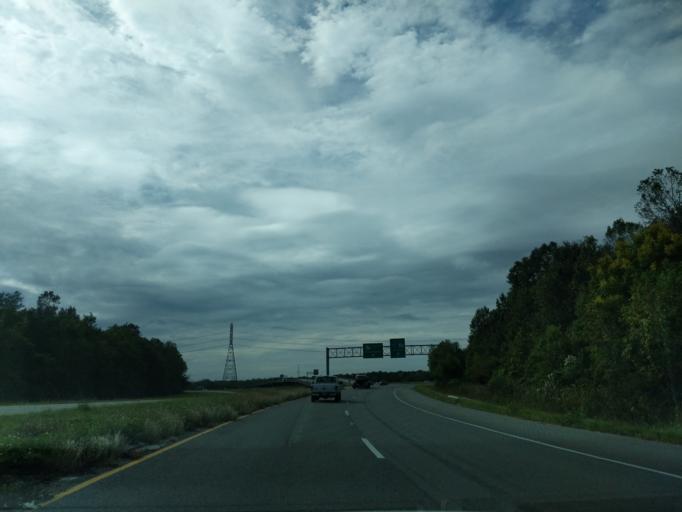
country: US
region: Louisiana
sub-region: Saint Bernard Parish
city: Chalmette
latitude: 30.0171
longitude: -89.9342
